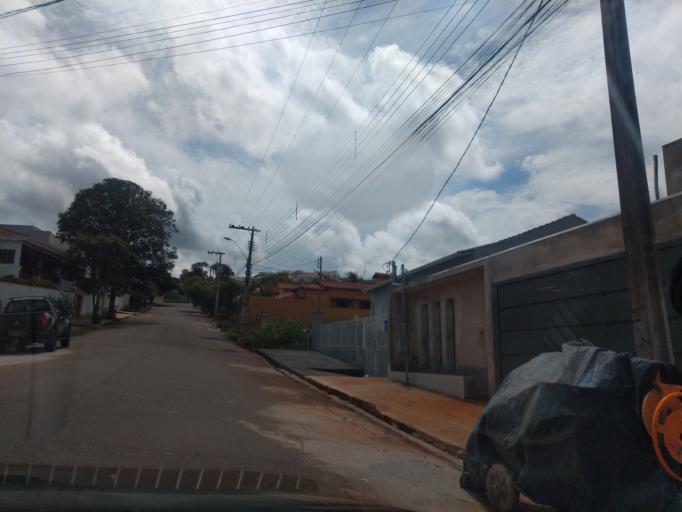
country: BR
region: Minas Gerais
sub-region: Tres Coracoes
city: Tres Coracoes
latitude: -21.6736
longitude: -45.2743
